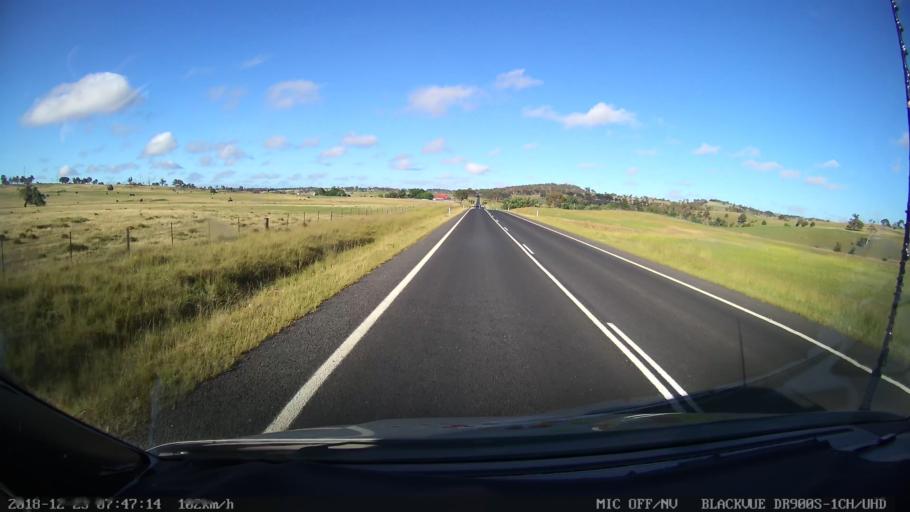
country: AU
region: New South Wales
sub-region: Armidale Dumaresq
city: Enmore
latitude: -30.5259
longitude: 151.9047
